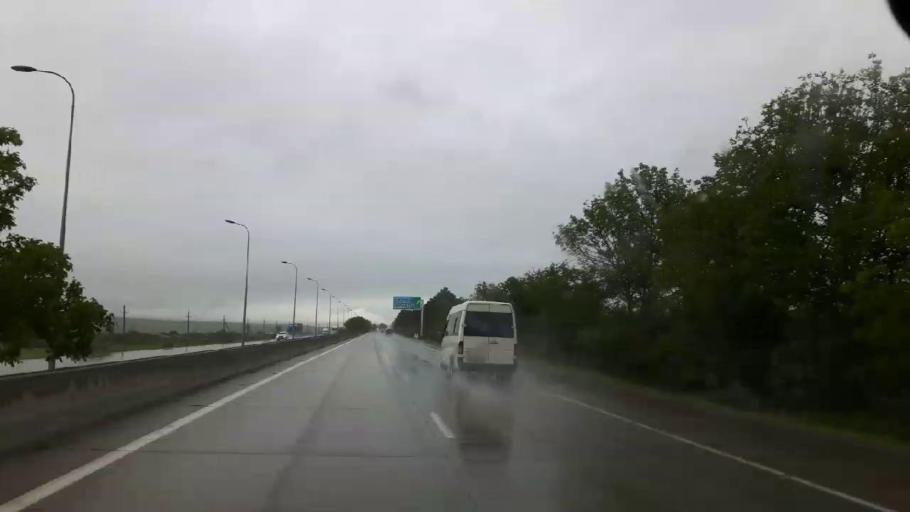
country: GE
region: Shida Kartli
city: Gori
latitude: 42.0230
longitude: 44.2815
